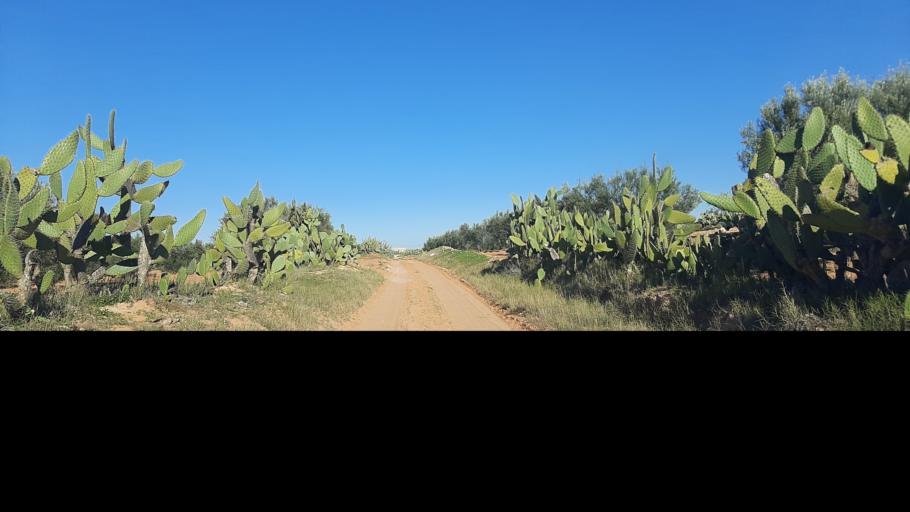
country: TN
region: Safaqis
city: Bi'r `Ali Bin Khalifah
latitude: 35.0244
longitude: 10.0746
